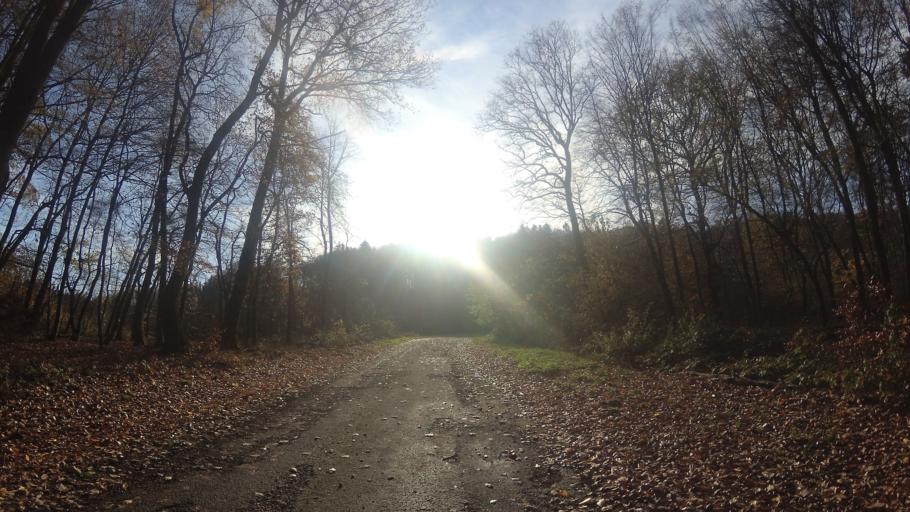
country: DE
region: Saarland
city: Freisen
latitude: 49.5436
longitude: 7.2539
